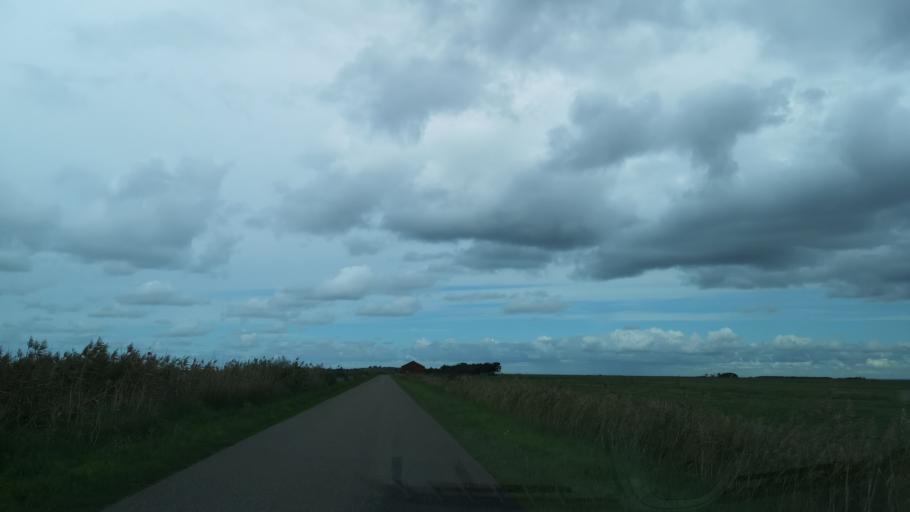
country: DK
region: Central Jutland
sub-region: Ringkobing-Skjern Kommune
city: Hvide Sande
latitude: 55.8382
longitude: 8.2175
